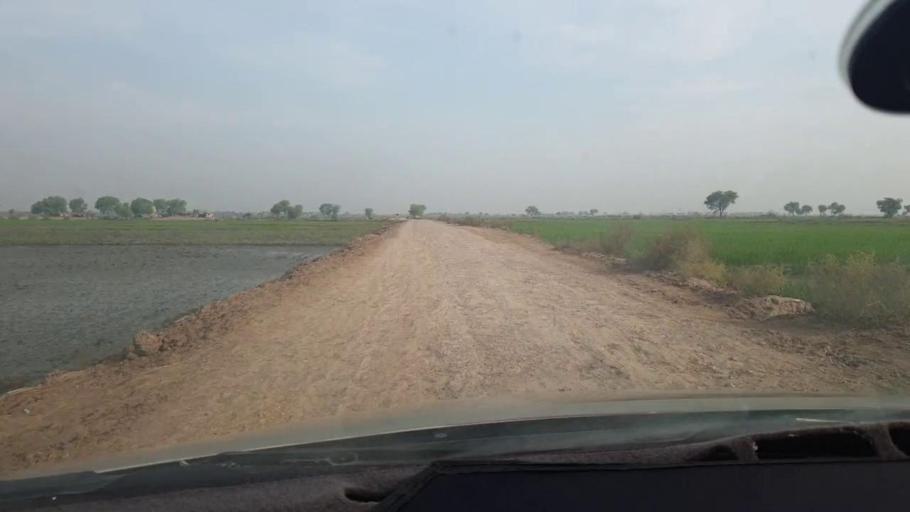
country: PK
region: Balochistan
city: Jhatpat
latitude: 28.3543
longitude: 68.4091
